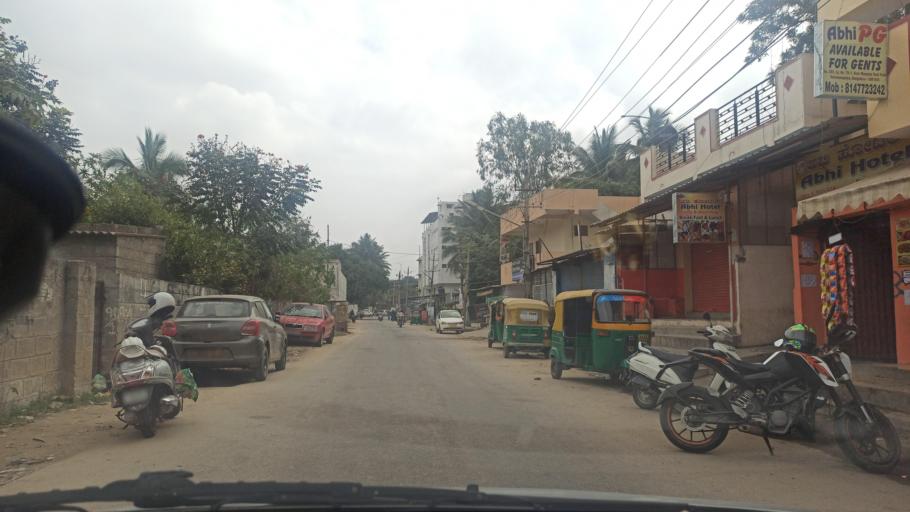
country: IN
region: Karnataka
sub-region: Bangalore Urban
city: Yelahanka
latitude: 13.0420
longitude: 77.6155
